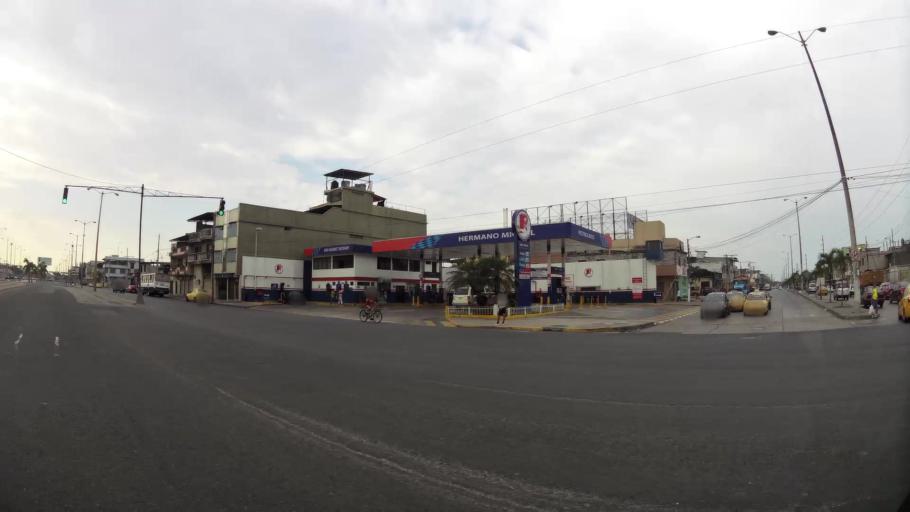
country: EC
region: Guayas
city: Guayaquil
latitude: -2.2513
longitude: -79.8944
